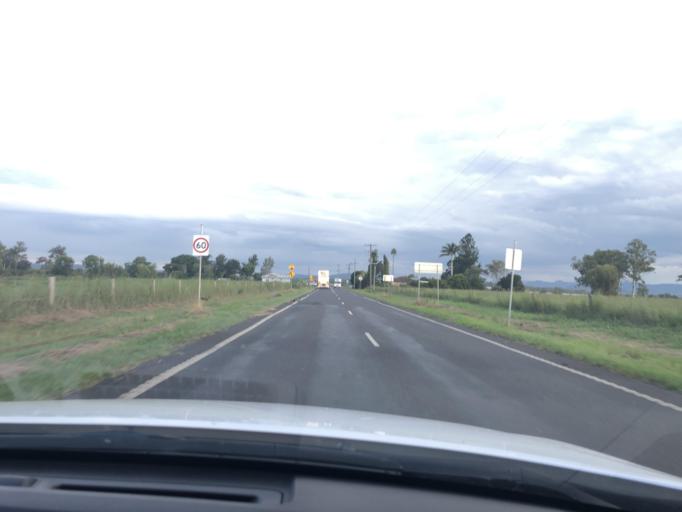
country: AU
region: Queensland
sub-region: Lockyer Valley
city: Gatton
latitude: -27.5816
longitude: 152.3628
